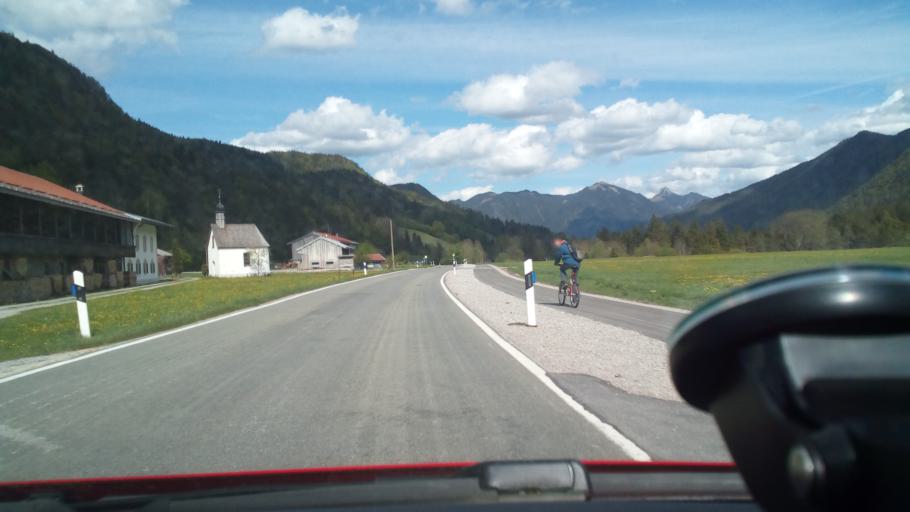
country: DE
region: Bavaria
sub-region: Upper Bavaria
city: Lenggries
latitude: 47.6272
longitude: 11.5140
